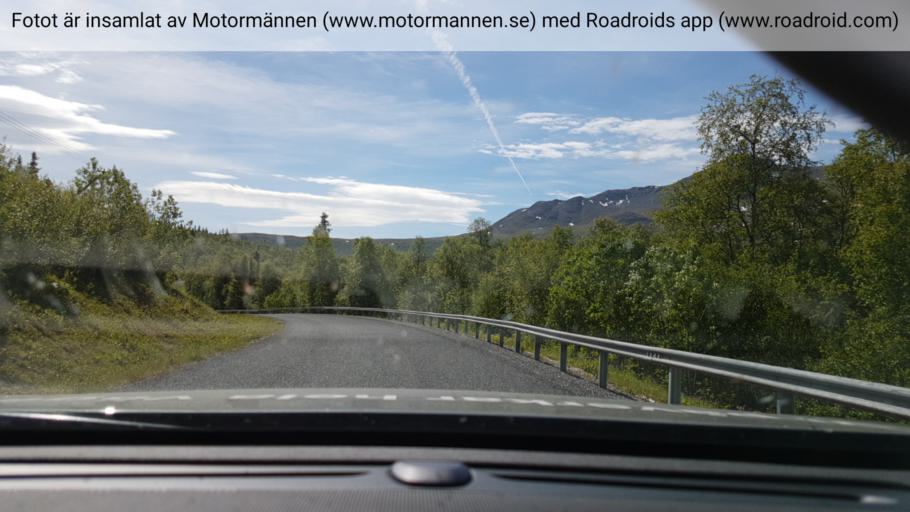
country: SE
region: Vaesterbotten
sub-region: Vilhelmina Kommun
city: Sjoberg
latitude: 65.3029
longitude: 15.2916
